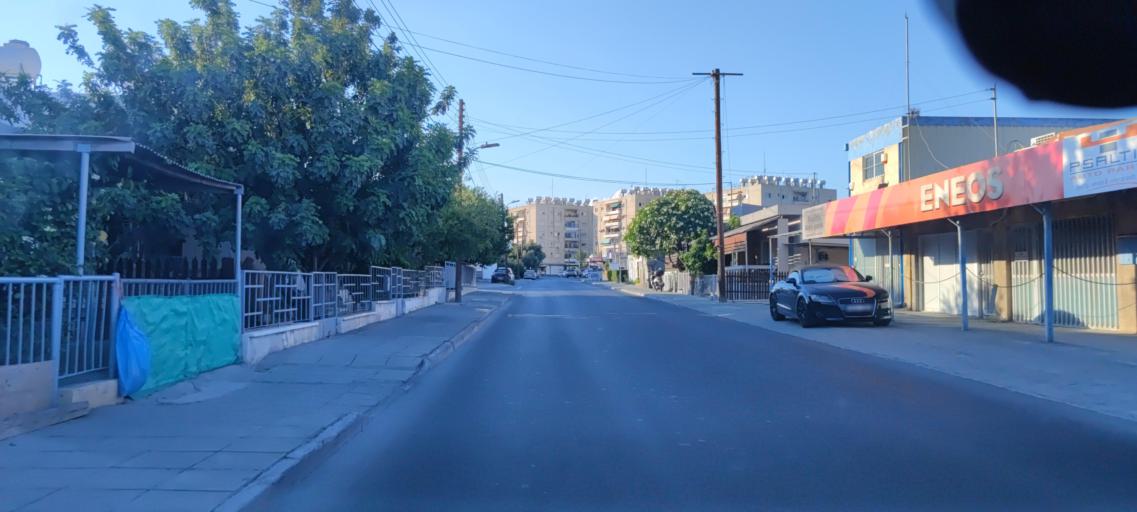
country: CY
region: Limassol
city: Limassol
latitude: 34.6762
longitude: 33.0288
